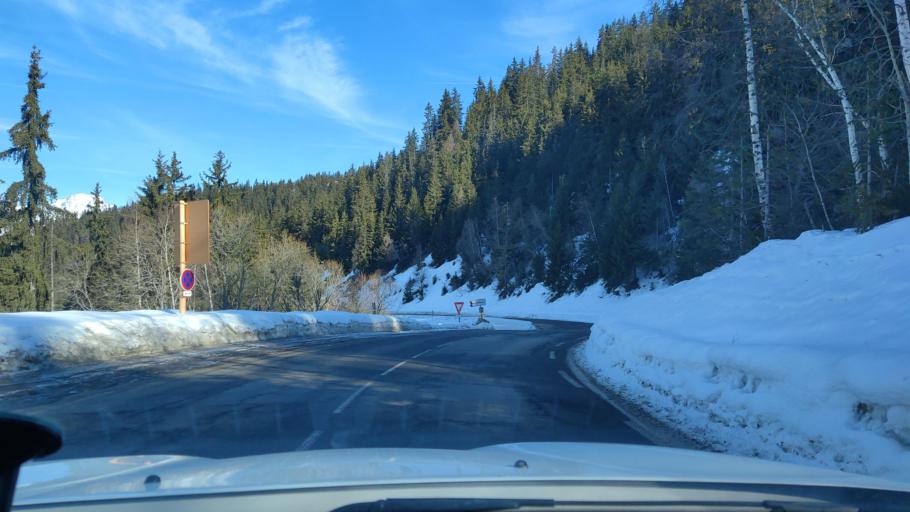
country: FR
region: Rhone-Alpes
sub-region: Departement de la Savoie
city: Bourg-Saint-Maurice
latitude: 45.5792
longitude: 6.7873
